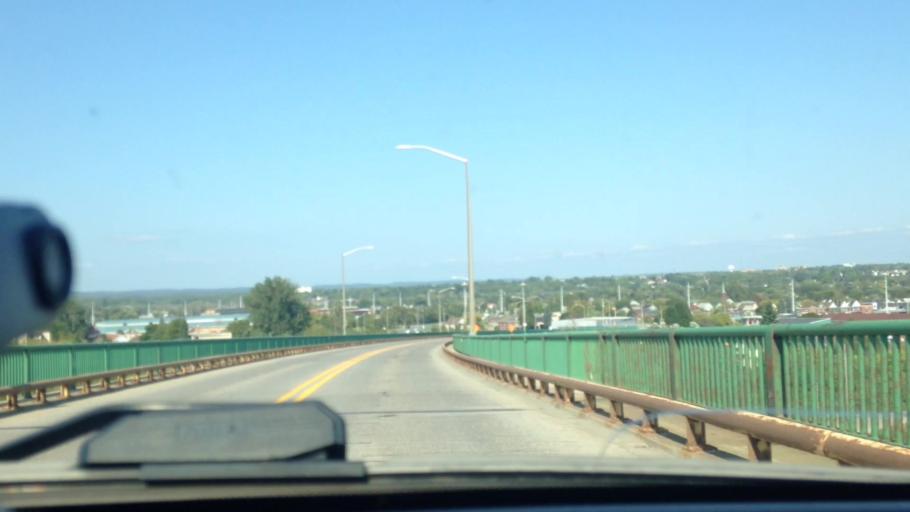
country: US
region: Michigan
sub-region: Chippewa County
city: Sault Ste. Marie
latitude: 46.5146
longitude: -84.3577
